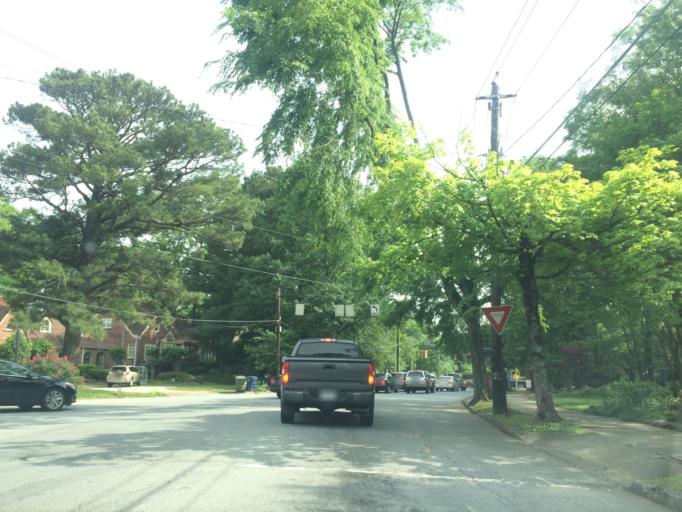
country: US
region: Georgia
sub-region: DeKalb County
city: Druid Hills
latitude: 33.7978
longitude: -84.3498
